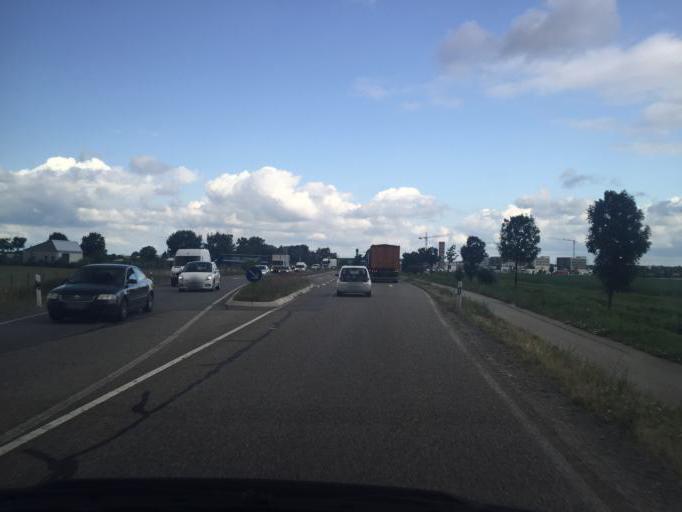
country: DE
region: Baden-Wuerttemberg
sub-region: Karlsruhe Region
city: Bruchsal
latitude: 49.1319
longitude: 8.5737
